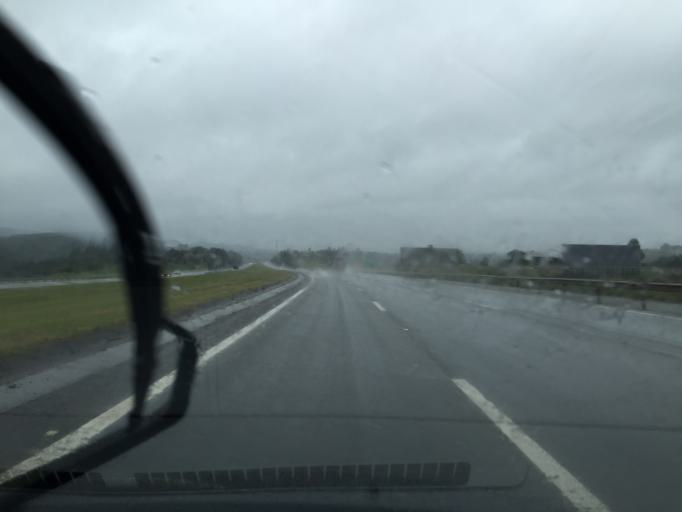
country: BR
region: Sao Paulo
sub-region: Mairinque
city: Mairinque
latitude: -23.4235
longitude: -47.2383
